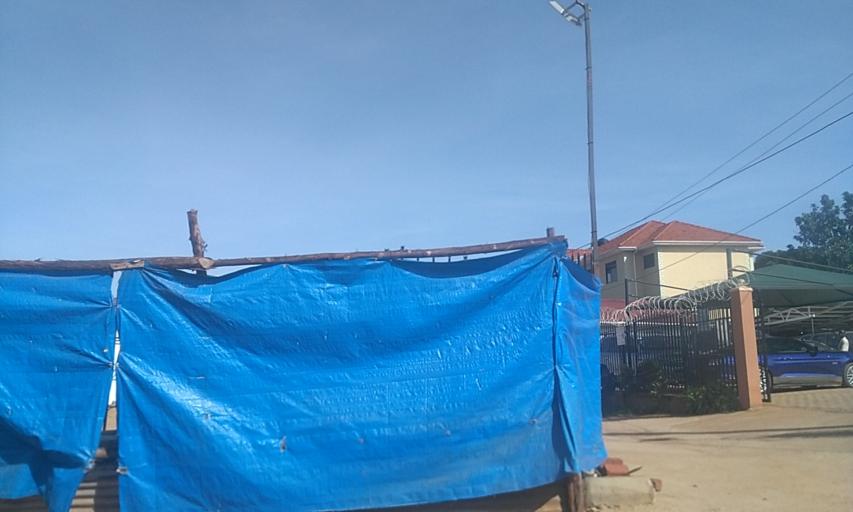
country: UG
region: Central Region
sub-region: Wakiso District
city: Kireka
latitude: 0.3742
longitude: 32.6249
